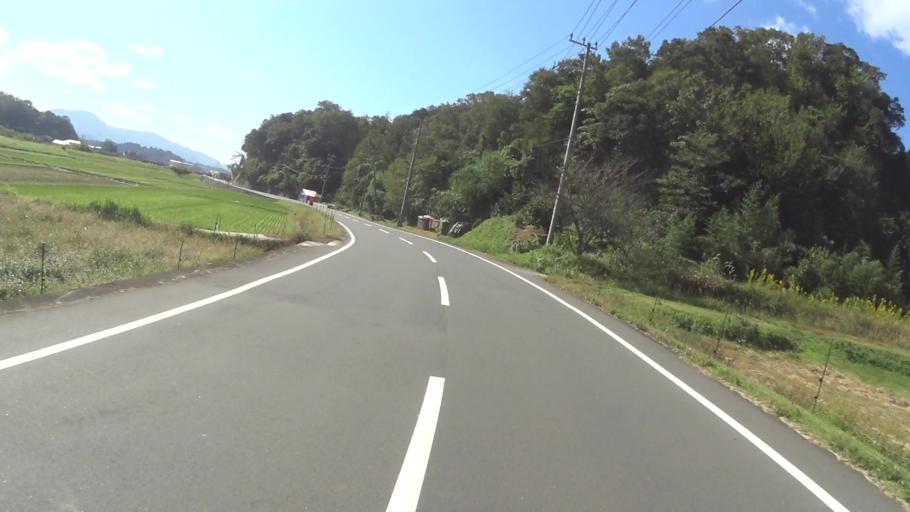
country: JP
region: Kyoto
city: Miyazu
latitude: 35.6923
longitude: 135.0971
